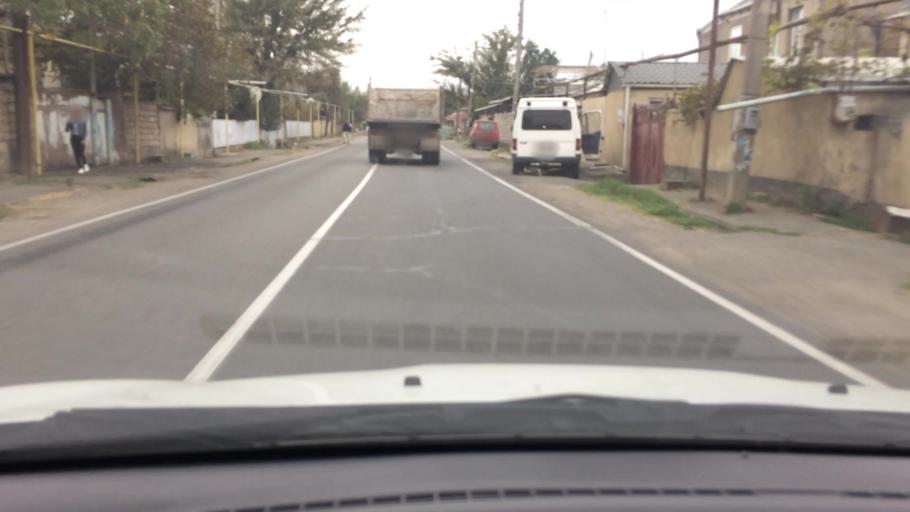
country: GE
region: Kvemo Kartli
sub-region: Marneuli
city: Marneuli
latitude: 41.4805
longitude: 44.7999
